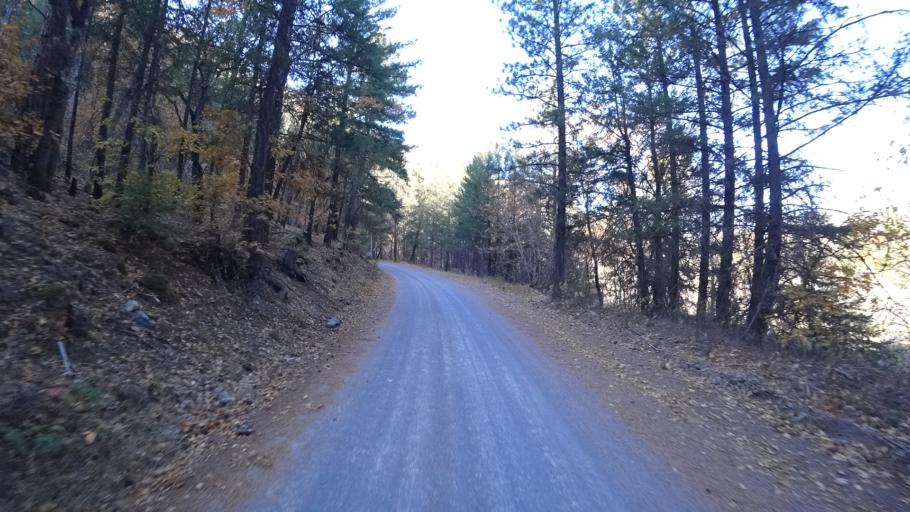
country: US
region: California
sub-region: Siskiyou County
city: Yreka
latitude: 41.8471
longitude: -122.6910
